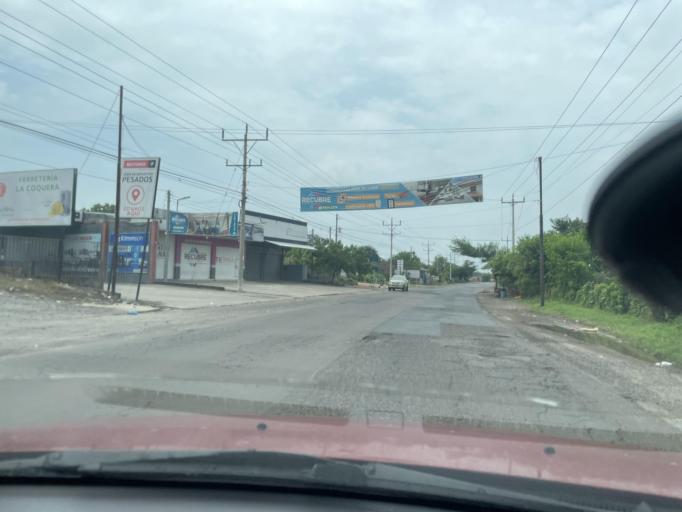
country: SV
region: La Union
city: Santa Rosa de Lima
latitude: 13.6265
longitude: -87.8708
